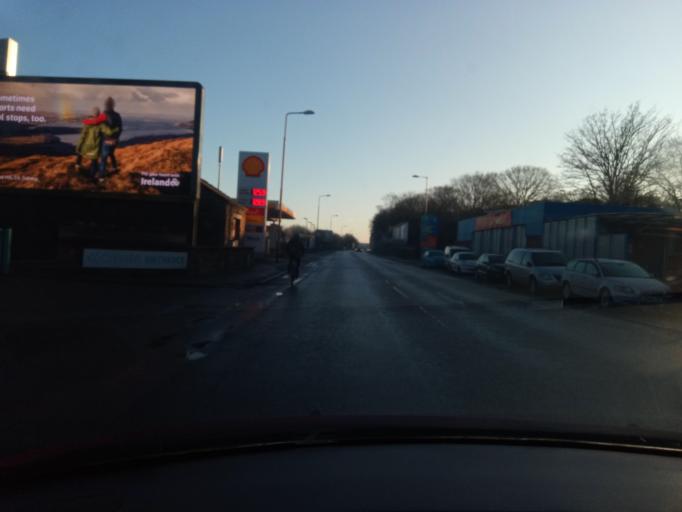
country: GB
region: Scotland
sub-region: West Lothian
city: Seafield
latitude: 55.9714
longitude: -3.1511
